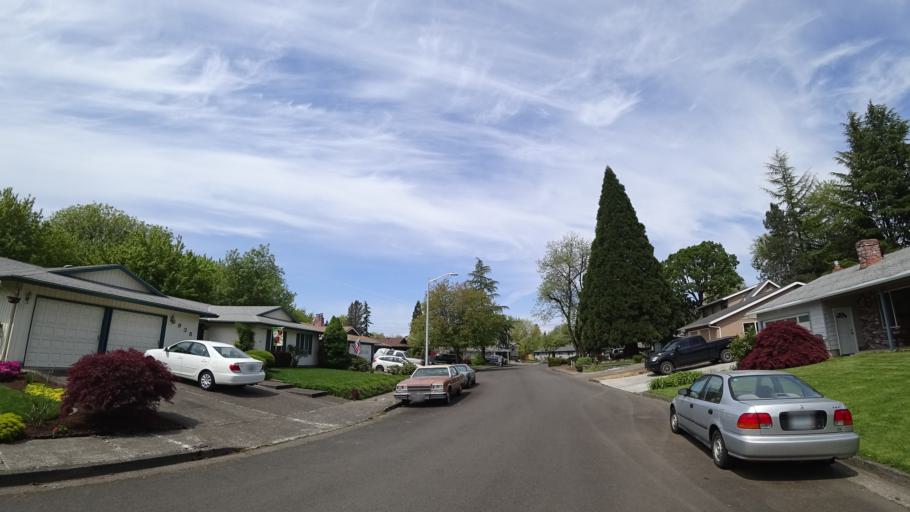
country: US
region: Oregon
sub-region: Washington County
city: Aloha
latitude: 45.4697
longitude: -122.8897
